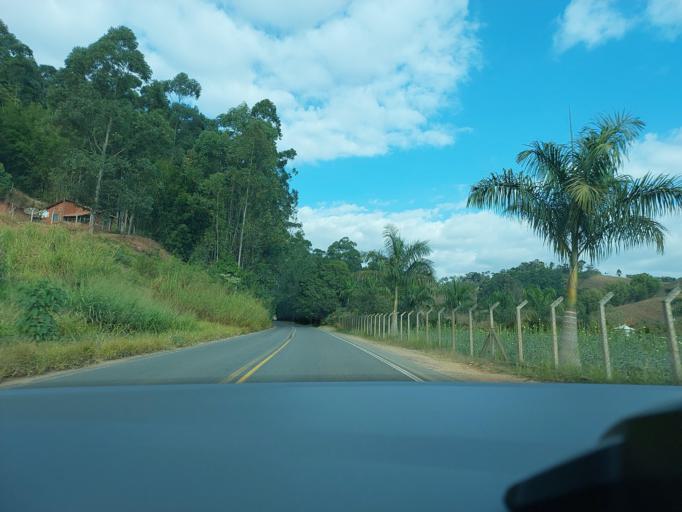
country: BR
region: Minas Gerais
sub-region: Vicosa
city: Vicosa
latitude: -20.8267
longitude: -42.7313
